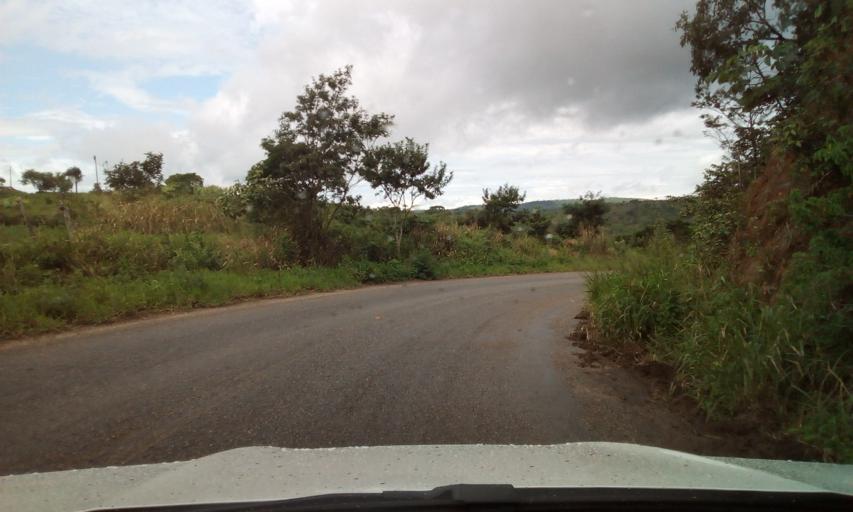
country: BR
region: Paraiba
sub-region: Areia
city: Areia
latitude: -6.9040
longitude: -35.6475
